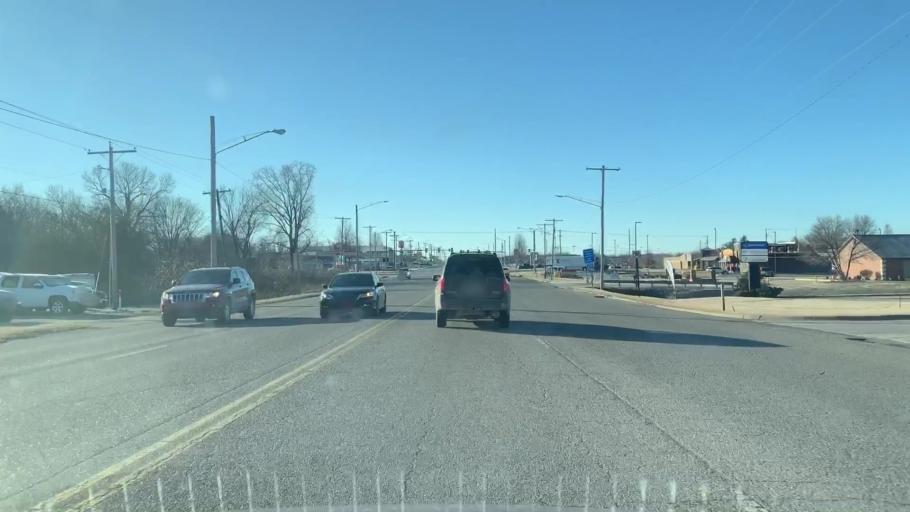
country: US
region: Kansas
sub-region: Crawford County
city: Frontenac
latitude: 37.4425
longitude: -94.7051
